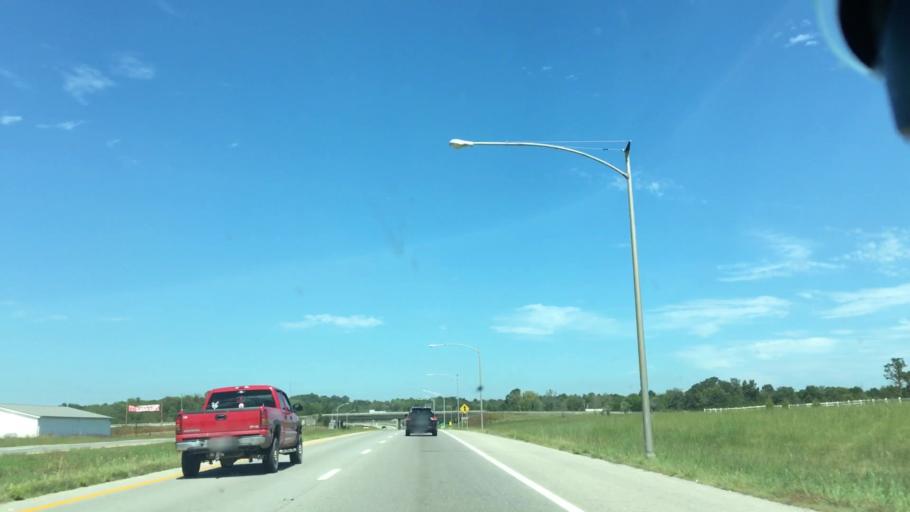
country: US
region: Kentucky
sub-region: Christian County
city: Hopkinsville
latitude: 36.8910
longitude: -87.4688
